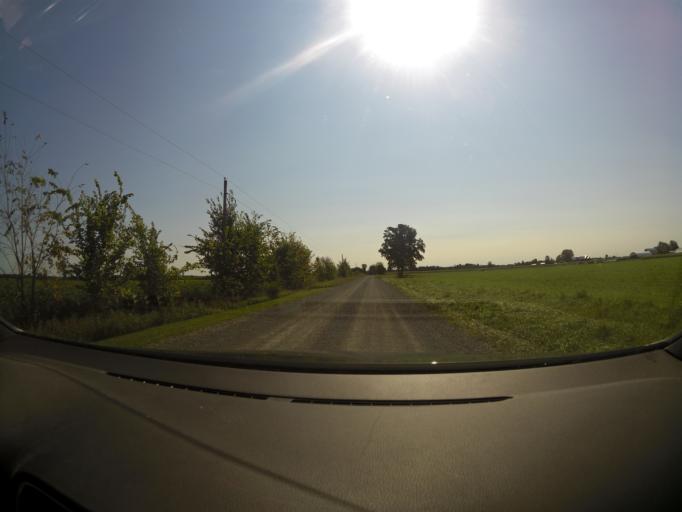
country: CA
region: Ontario
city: Arnprior
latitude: 45.3607
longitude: -76.2922
